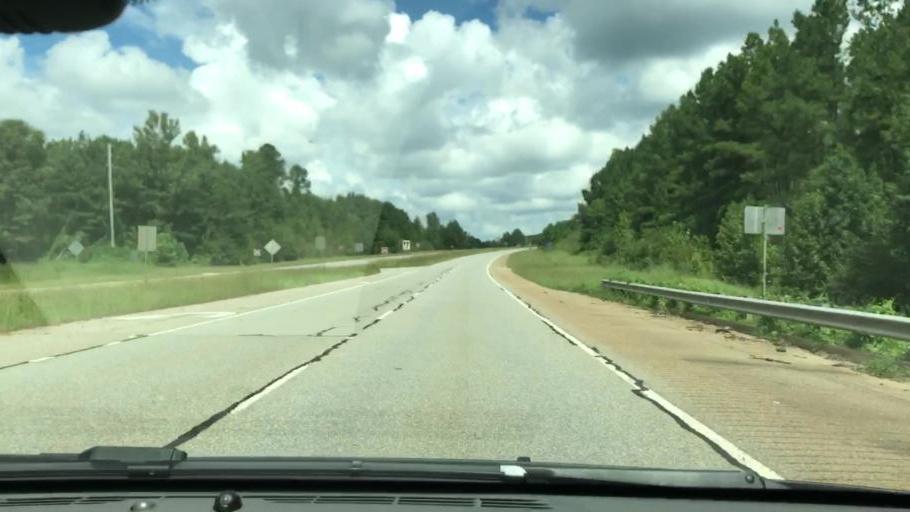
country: US
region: Georgia
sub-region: Stewart County
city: Lumpkin
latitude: 32.1041
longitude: -84.8123
